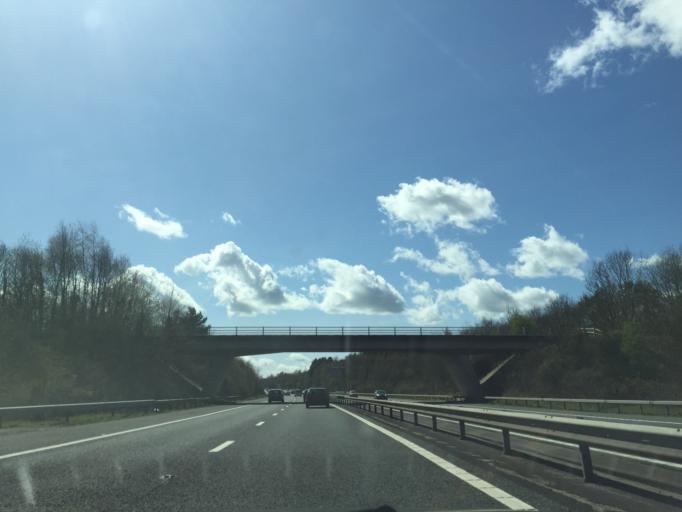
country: GB
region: England
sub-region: Hampshire
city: Waterlooville
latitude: 50.8762
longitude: -1.0129
